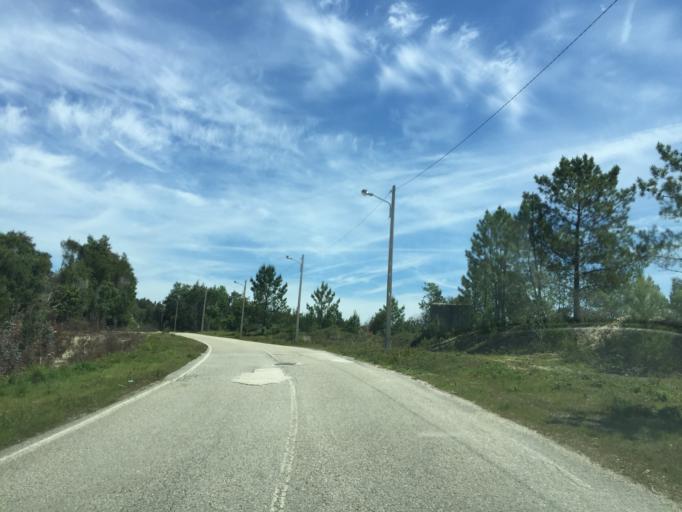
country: PT
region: Coimbra
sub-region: Soure
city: Soure
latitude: 40.0611
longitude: -8.6919
